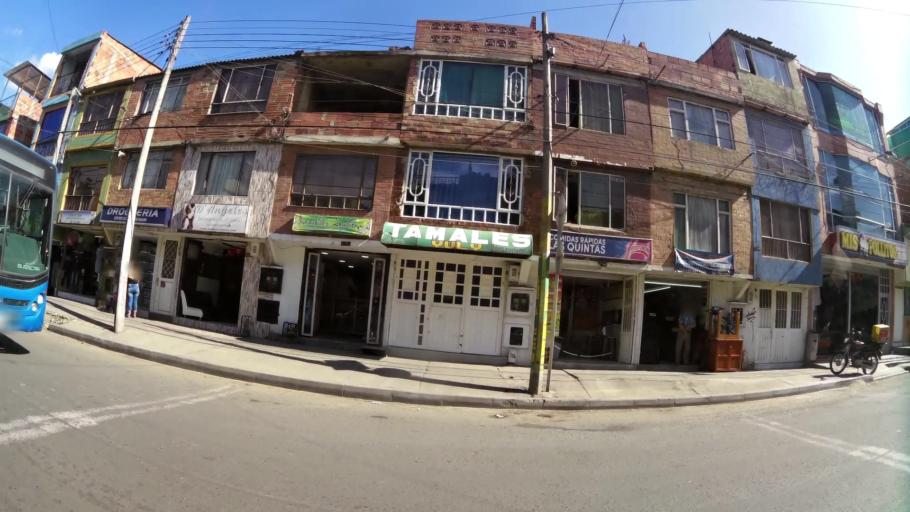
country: CO
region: Cundinamarca
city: Soacha
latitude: 4.5467
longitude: -74.1390
